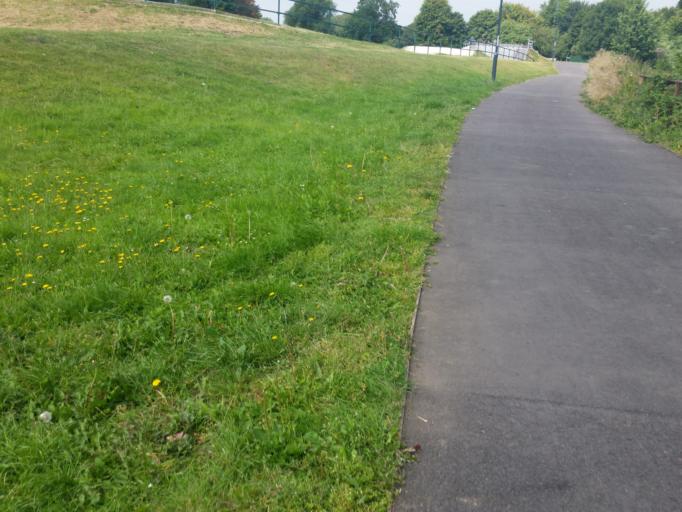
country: GB
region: England
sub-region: Derby
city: Derby
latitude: 52.9049
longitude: -1.4338
